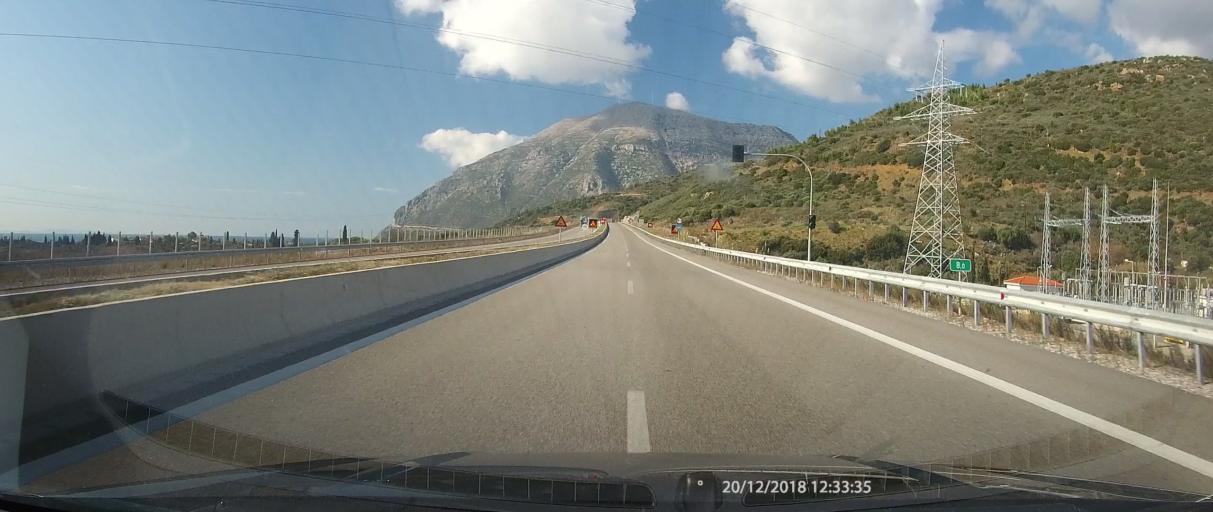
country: GR
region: West Greece
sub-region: Nomos Aitolias kai Akarnanias
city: Antirrio
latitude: 38.3513
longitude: 21.7376
